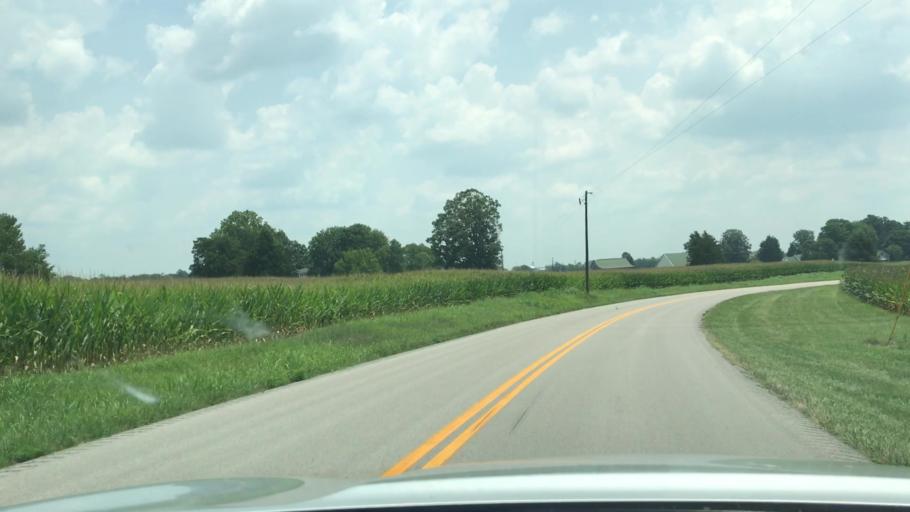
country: US
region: Kentucky
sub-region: Todd County
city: Elkton
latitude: 36.7593
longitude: -87.0976
